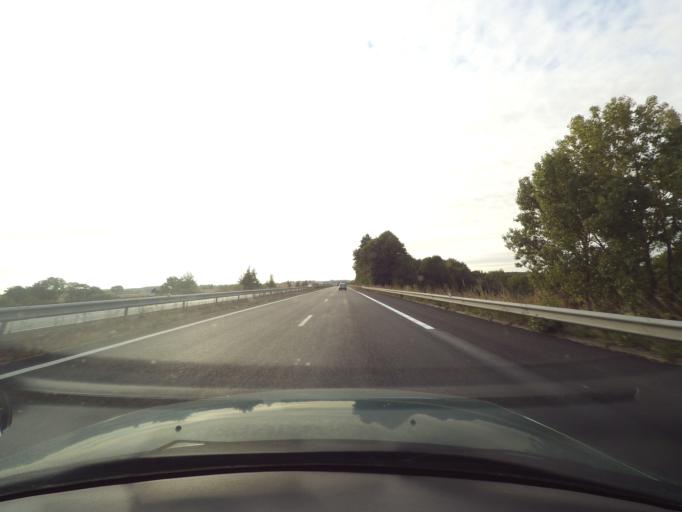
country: FR
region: Pays de la Loire
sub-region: Departement de Maine-et-Loire
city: La Seguiniere
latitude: 47.0788
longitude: -0.9601
